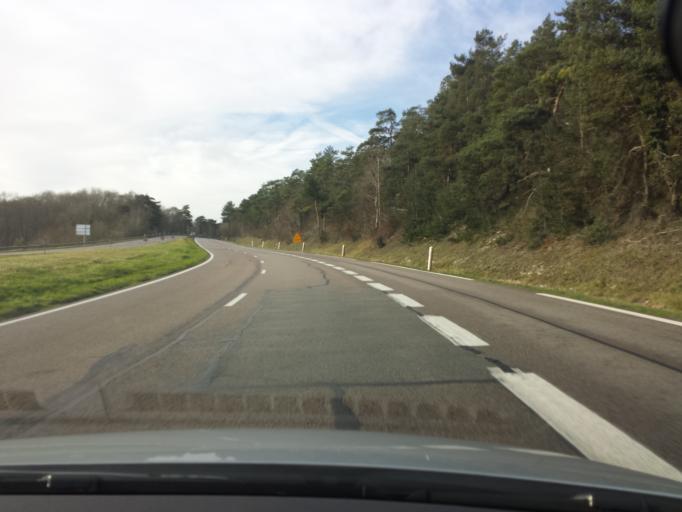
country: FR
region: Haute-Normandie
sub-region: Departement de l'Eure
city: Menilles
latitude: 49.0140
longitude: 1.3444
